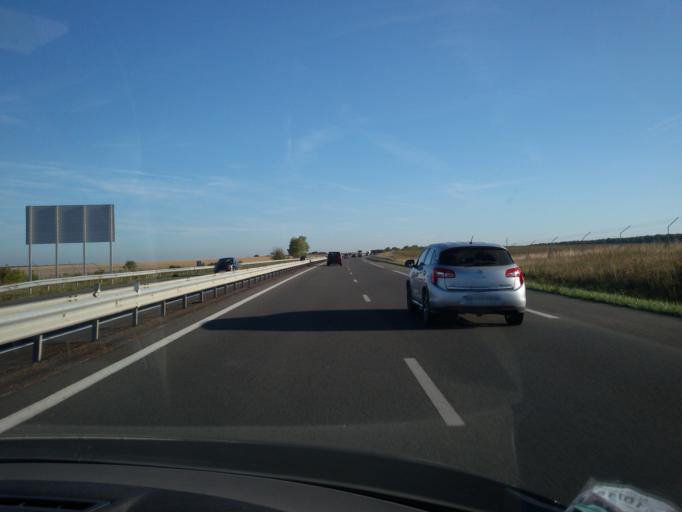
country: FR
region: Centre
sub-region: Departement du Cher
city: Levet
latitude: 46.8316
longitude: 2.4128
